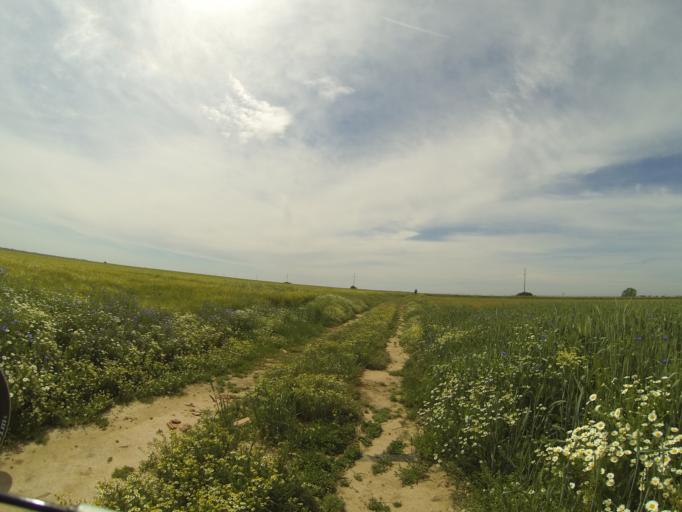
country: RO
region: Dolj
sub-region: Comuna Ghindeni
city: Ghindeni
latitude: 44.2166
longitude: 23.9391
